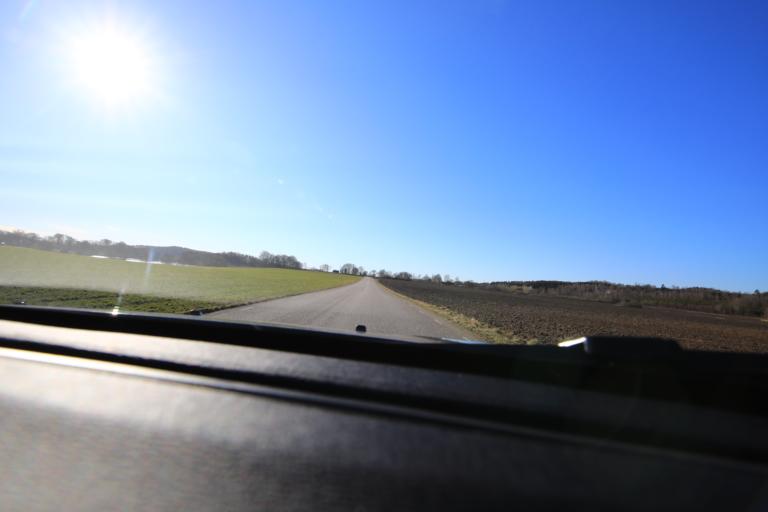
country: SE
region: Halland
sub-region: Varbergs Kommun
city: Tvaaker
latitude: 57.0602
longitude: 12.4490
